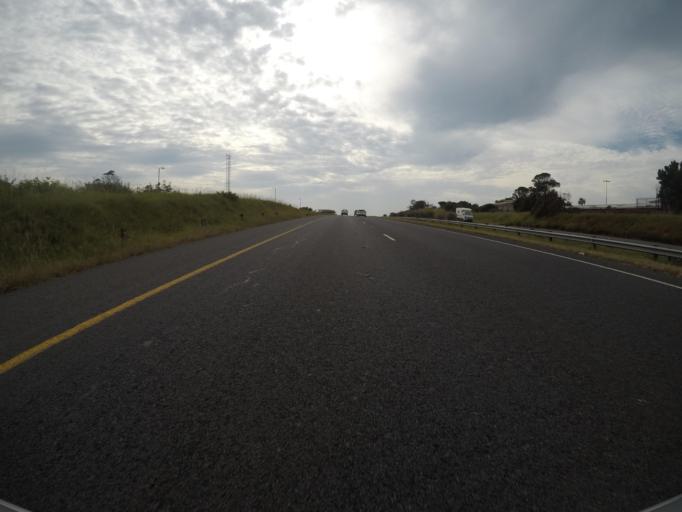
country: ZA
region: Eastern Cape
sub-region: Buffalo City Metropolitan Municipality
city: East London
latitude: -32.9708
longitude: 27.8868
